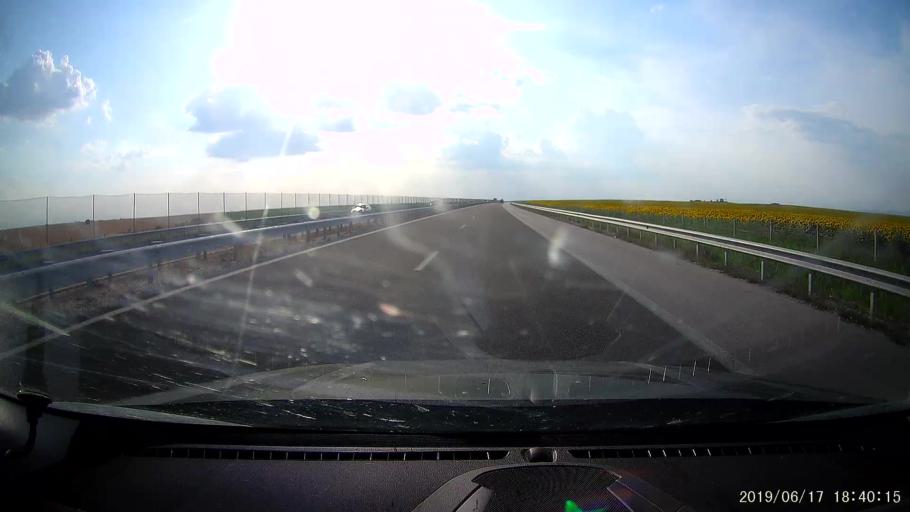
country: BG
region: Stara Zagora
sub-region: Obshtina Chirpan
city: Chirpan
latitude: 42.1533
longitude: 25.2829
